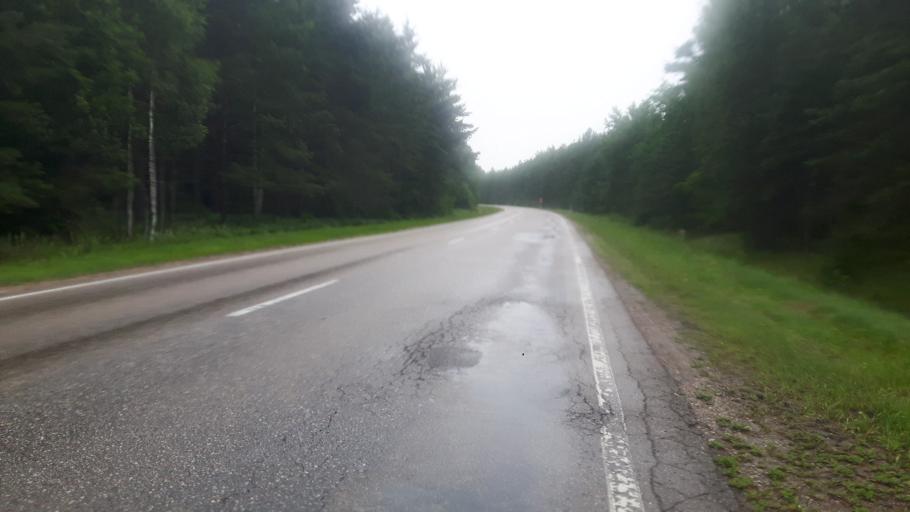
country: LV
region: Rucavas
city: Rucava
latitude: 56.1357
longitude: 21.1518
